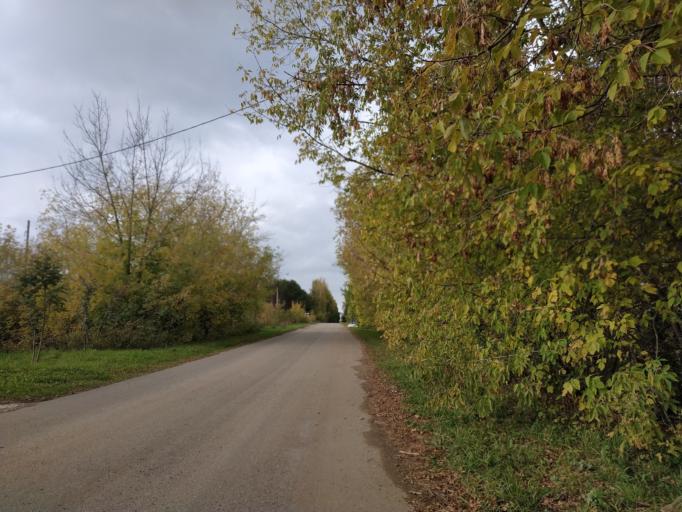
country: RU
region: Chuvashia
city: Ishley
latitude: 56.1268
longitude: 47.0922
